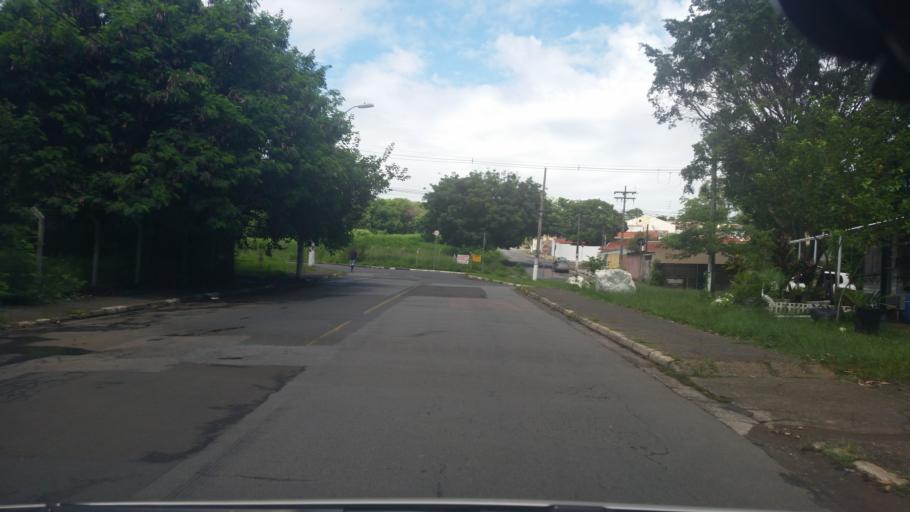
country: BR
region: Sao Paulo
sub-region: Campinas
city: Campinas
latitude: -22.8539
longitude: -47.0608
